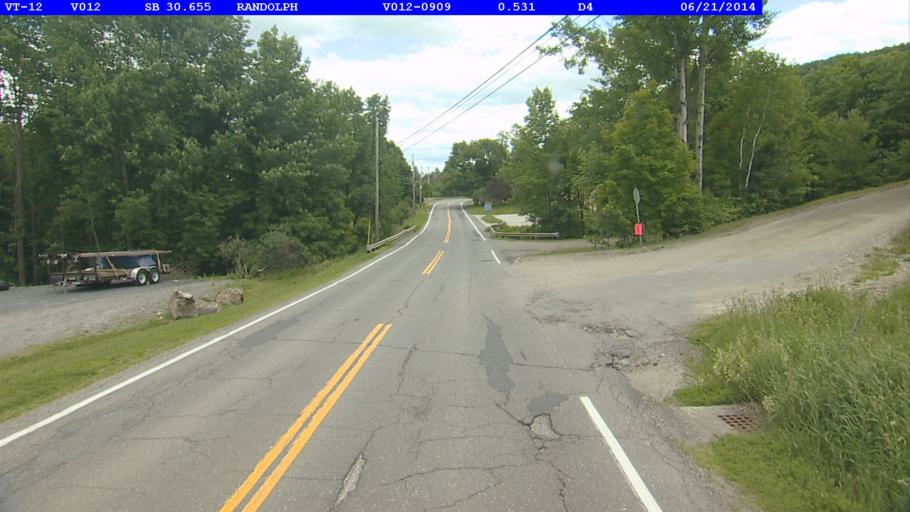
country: US
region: Vermont
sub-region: Orange County
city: Randolph
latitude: 43.9019
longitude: -72.6570
